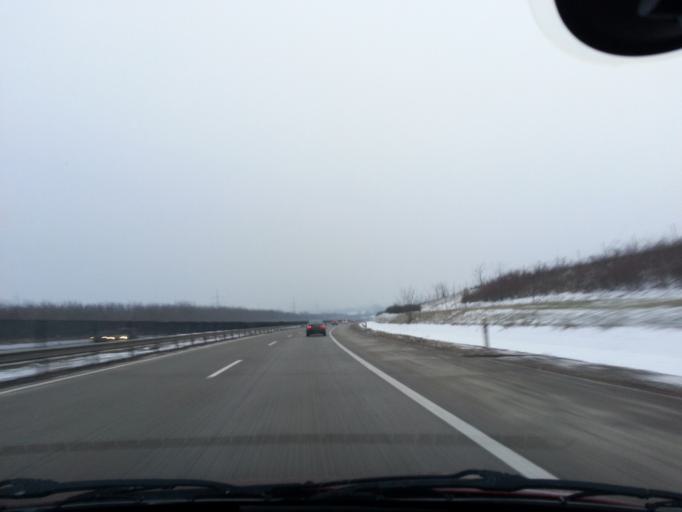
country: HU
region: Pest
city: Ecser
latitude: 47.4516
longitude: 19.3314
